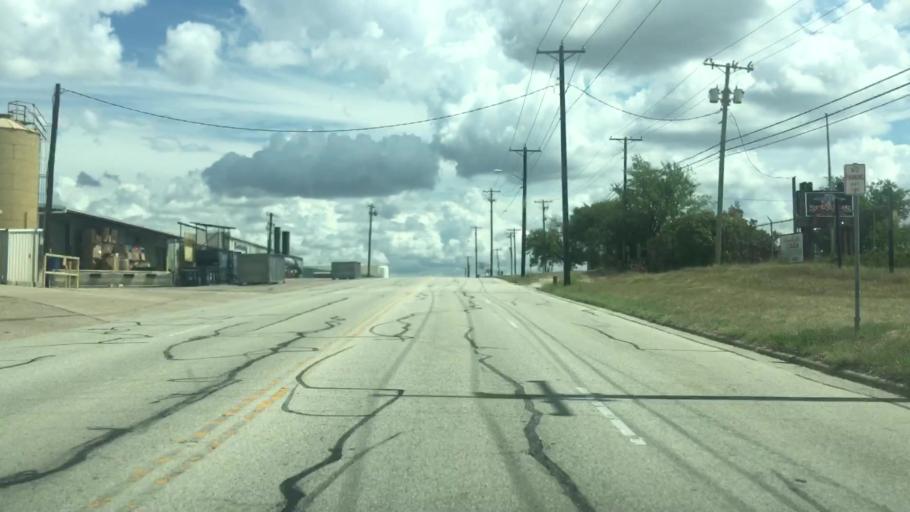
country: US
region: Texas
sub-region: Bell County
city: Temple
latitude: 31.1281
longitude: -97.3476
